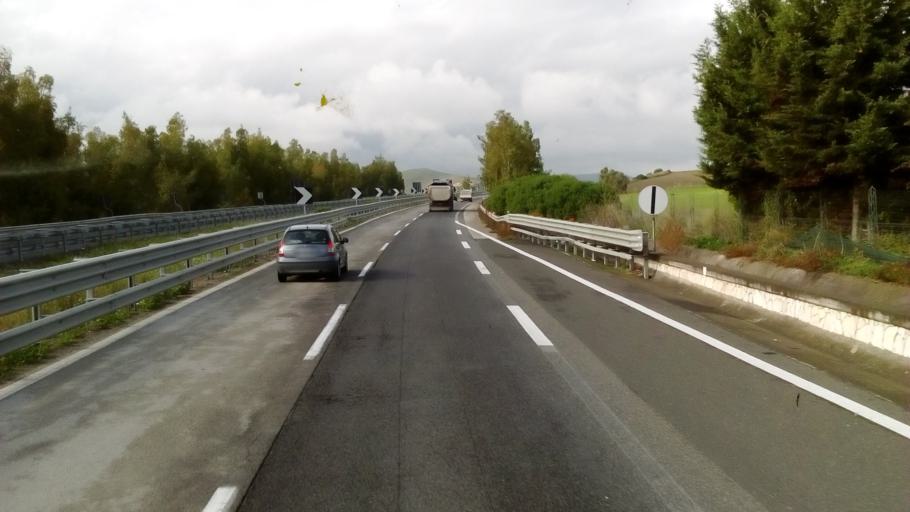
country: IT
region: Sicily
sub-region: Enna
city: Assoro
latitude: 37.5704
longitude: 14.4707
